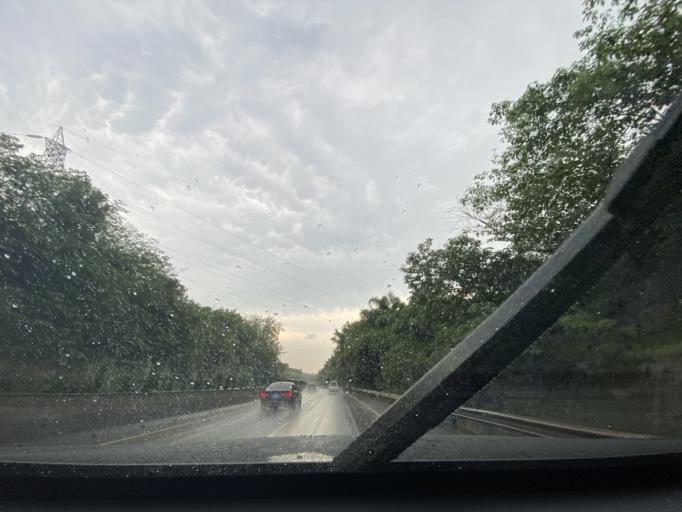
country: CN
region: Sichuan
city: Chonglong
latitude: 29.7631
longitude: 104.8178
